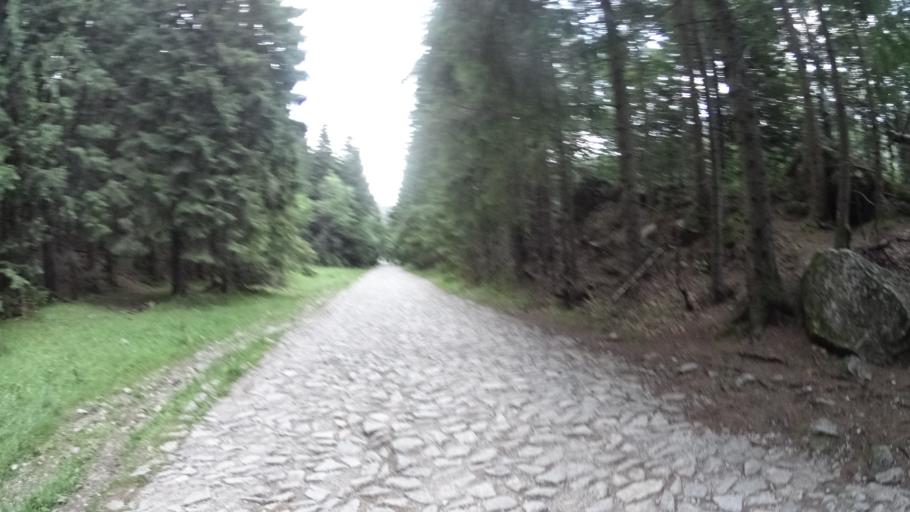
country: PL
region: Lesser Poland Voivodeship
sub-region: Powiat tatrzanski
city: Zakopane
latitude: 49.2650
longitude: 19.9752
